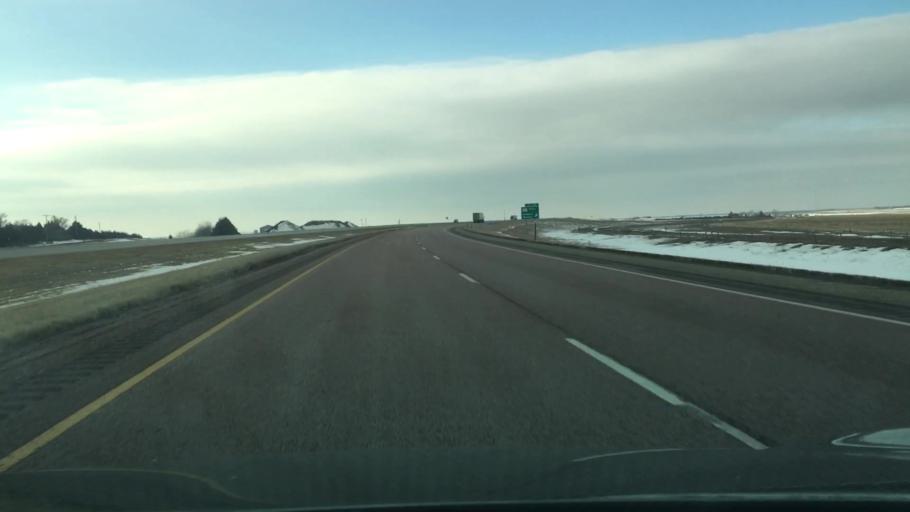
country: US
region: South Dakota
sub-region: Brule County
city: Chamberlain
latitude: 43.8465
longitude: -99.5572
